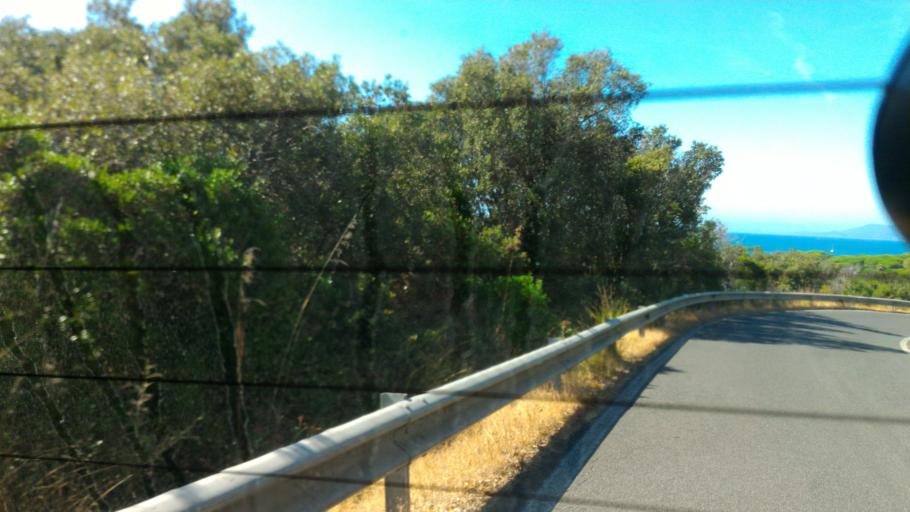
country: IT
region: Tuscany
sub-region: Provincia di Grosseto
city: Porto Ercole
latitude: 42.4300
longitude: 11.1706
